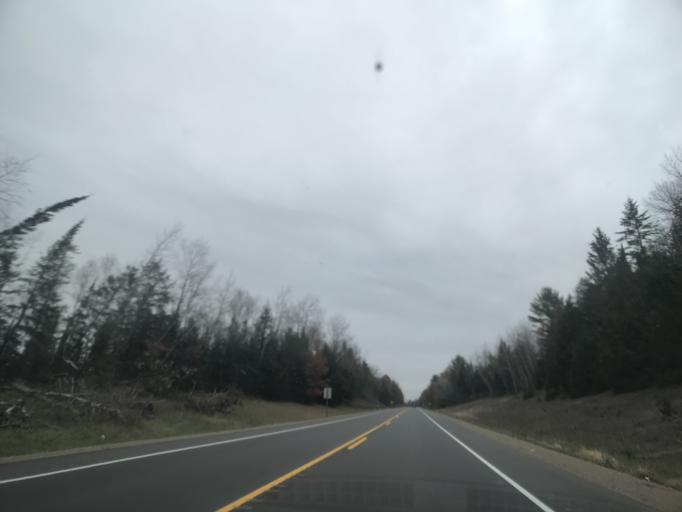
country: US
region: Wisconsin
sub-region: Menominee County
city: Legend Lake
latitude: 45.2653
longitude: -88.5122
